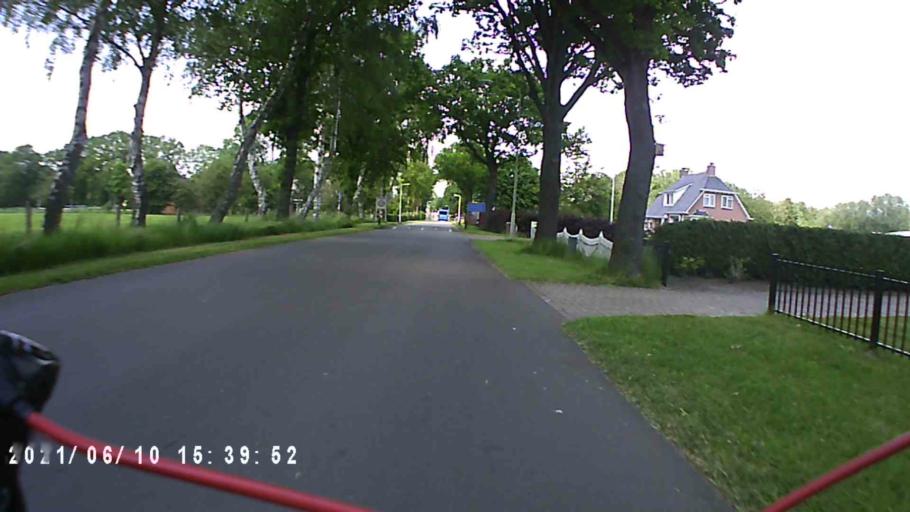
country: NL
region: Friesland
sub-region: Gemeente Achtkarspelen
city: Boelenslaan
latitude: 53.1587
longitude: 6.1478
